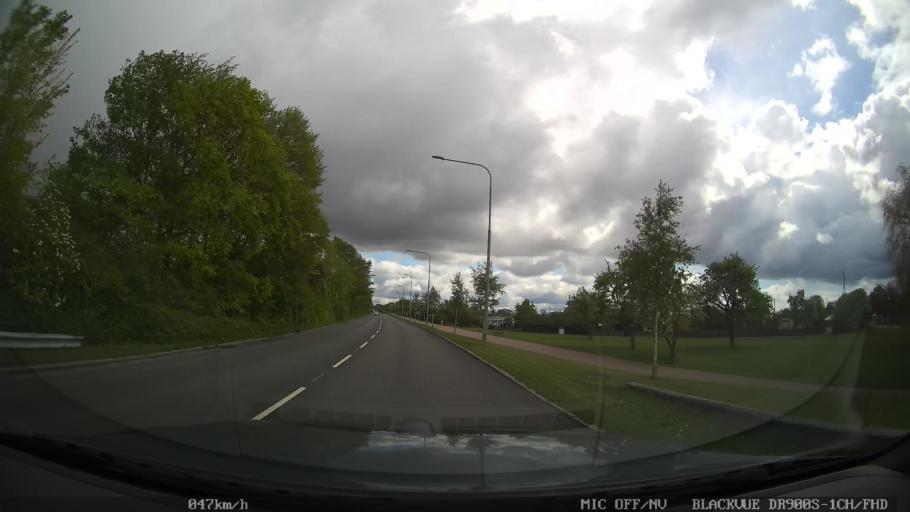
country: SE
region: Skane
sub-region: Landskrona
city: Landskrona
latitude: 55.8882
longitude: 12.8200
